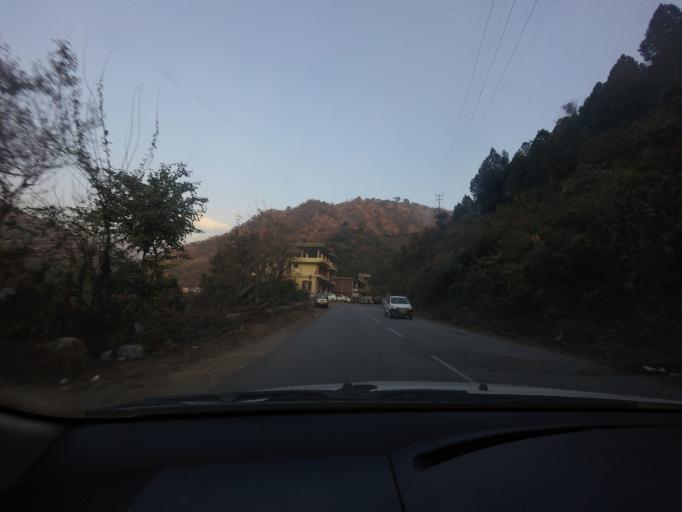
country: IN
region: Himachal Pradesh
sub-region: Mandi
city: Mandi
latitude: 31.7020
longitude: 76.9734
